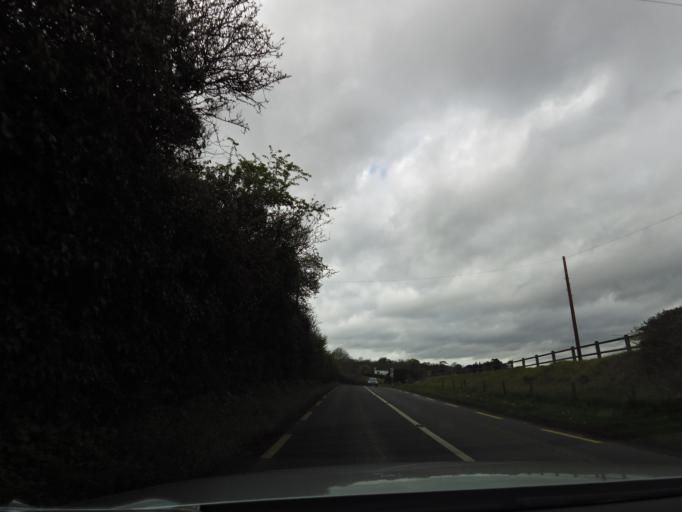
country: IE
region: Leinster
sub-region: Kilkenny
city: Kilkenny
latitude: 52.6761
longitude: -7.2736
